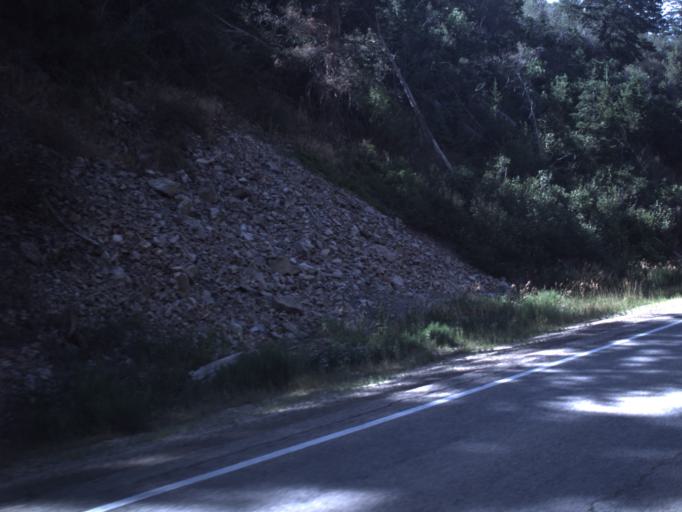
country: US
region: Utah
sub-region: Wasatch County
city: Heber
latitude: 40.3741
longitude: -111.2946
